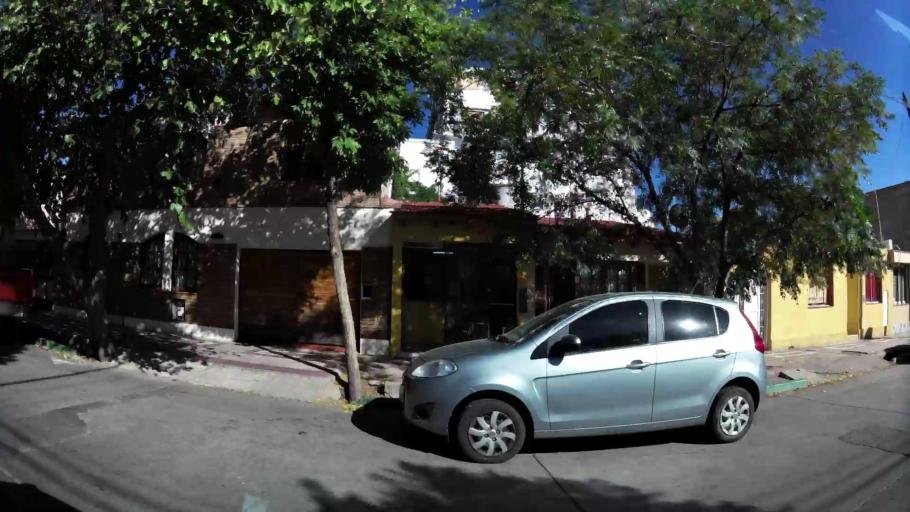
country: AR
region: Mendoza
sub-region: Departamento de Godoy Cruz
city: Godoy Cruz
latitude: -32.9246
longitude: -68.8429
